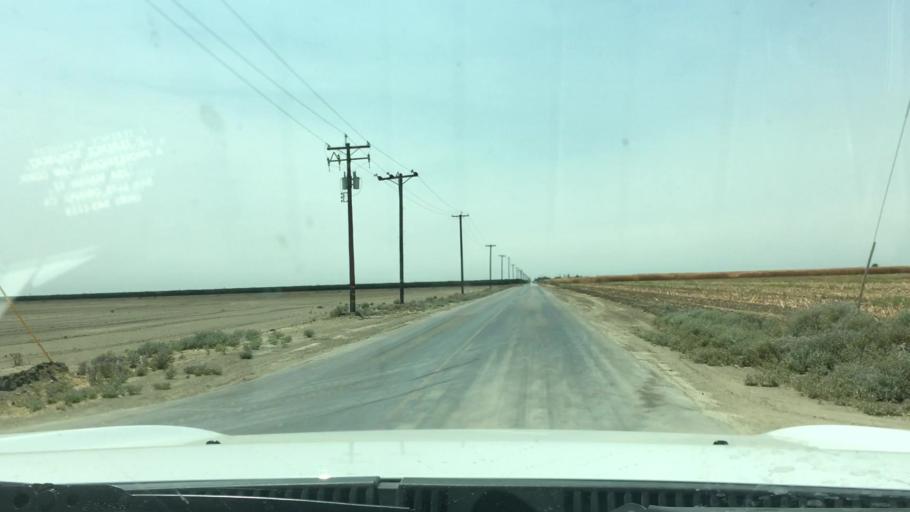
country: US
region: California
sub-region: Kern County
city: Wasco
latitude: 35.7029
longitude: -119.4373
